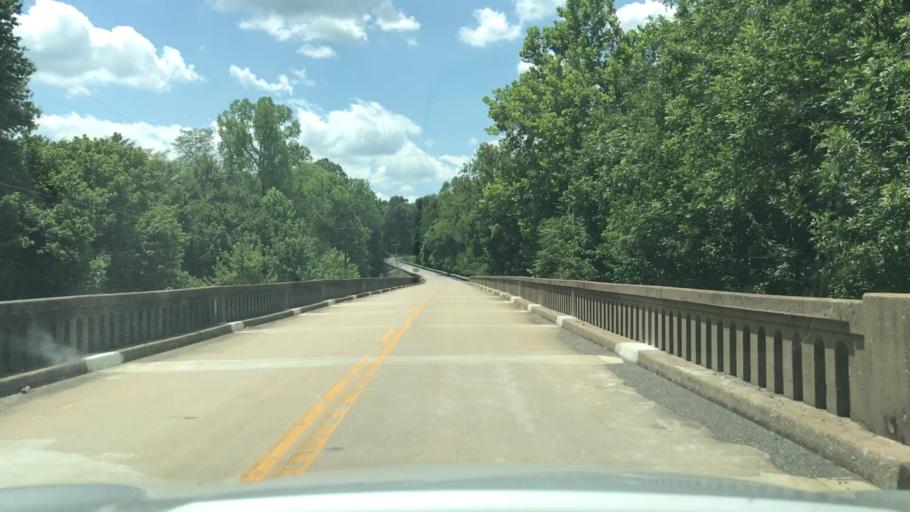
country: US
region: Kentucky
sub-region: Hopkins County
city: Nortonville
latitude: 37.1225
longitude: -87.3189
